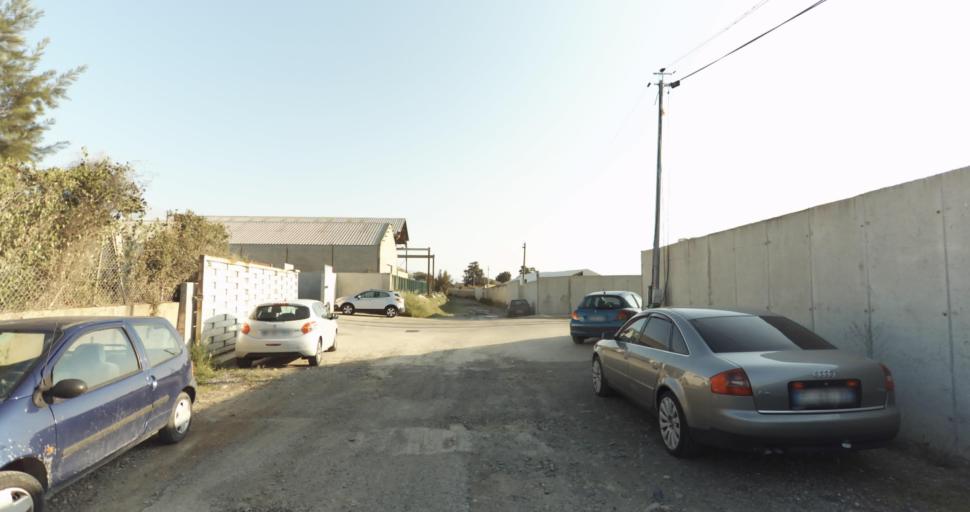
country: FR
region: Corsica
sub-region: Departement de la Haute-Corse
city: Biguglia
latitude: 42.5995
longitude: 9.4460
